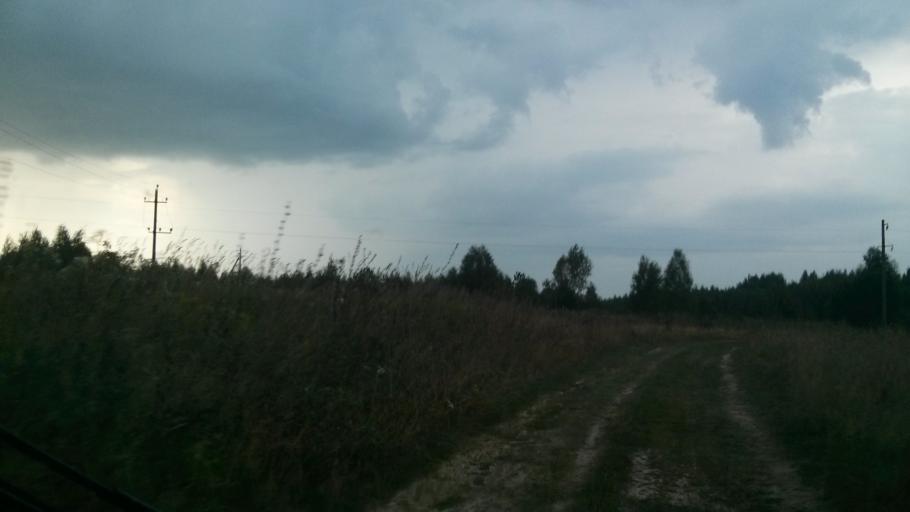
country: RU
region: Nizjnij Novgorod
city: Shimorskoye
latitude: 55.3142
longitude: 41.8630
